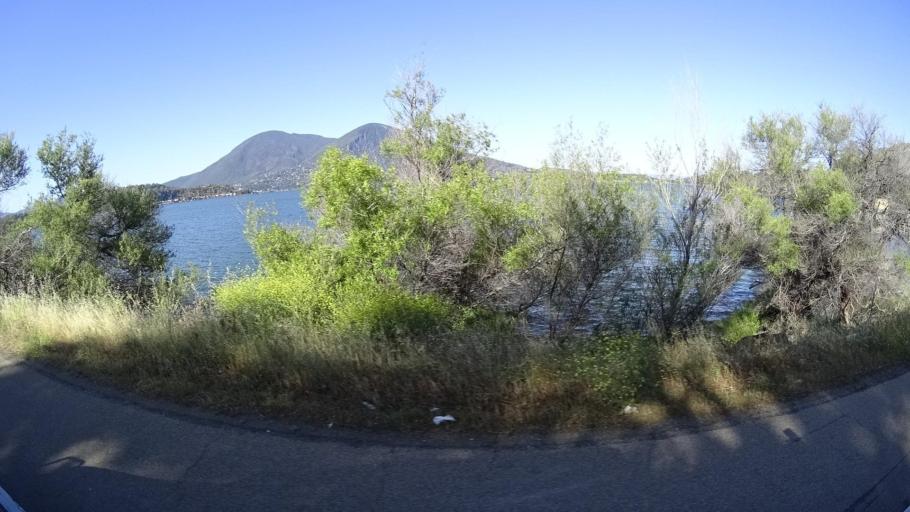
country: US
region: California
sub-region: Lake County
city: Clearlake Oaks
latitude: 39.0224
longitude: -122.7177
